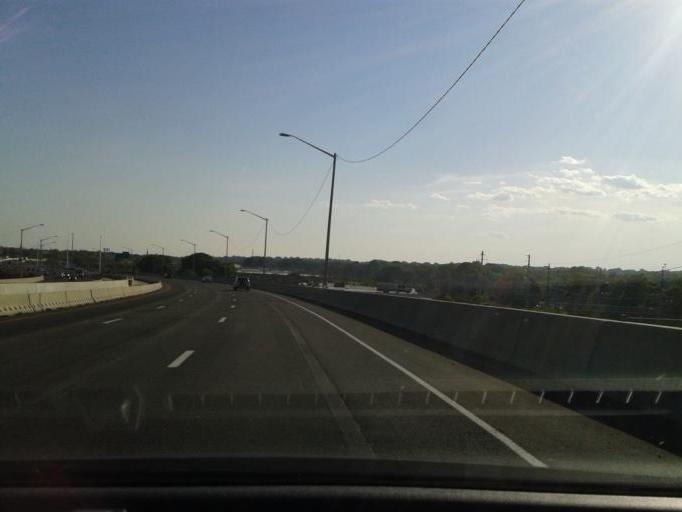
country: US
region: Connecticut
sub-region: Fairfield County
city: Stratford
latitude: 41.2045
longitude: -73.1121
